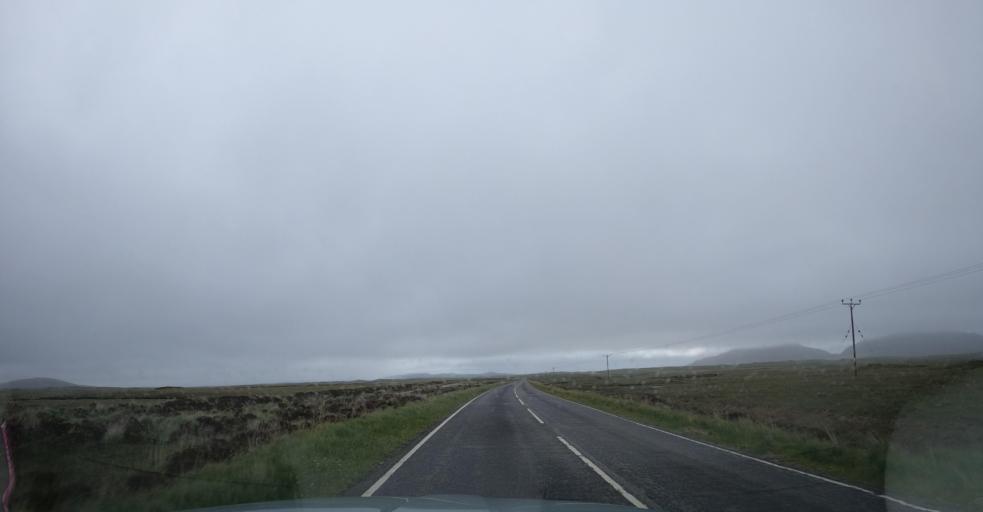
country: GB
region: Scotland
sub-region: Eilean Siar
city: Isle of North Uist
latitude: 57.5915
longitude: -7.2206
